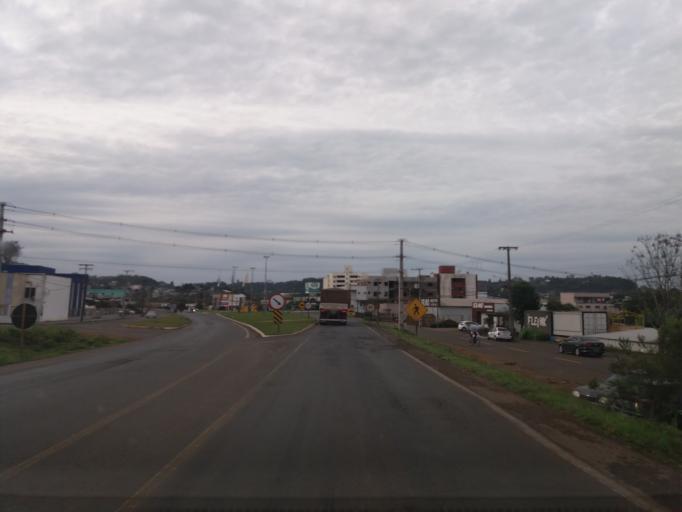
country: BR
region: Parana
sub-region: Francisco Beltrao
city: Francisco Beltrao
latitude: -26.0807
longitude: -53.0700
